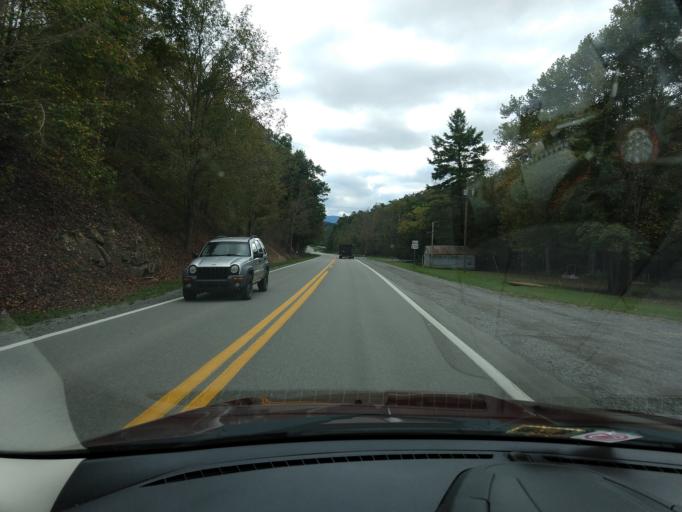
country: US
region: West Virginia
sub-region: Barbour County
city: Belington
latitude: 39.0466
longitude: -79.9581
